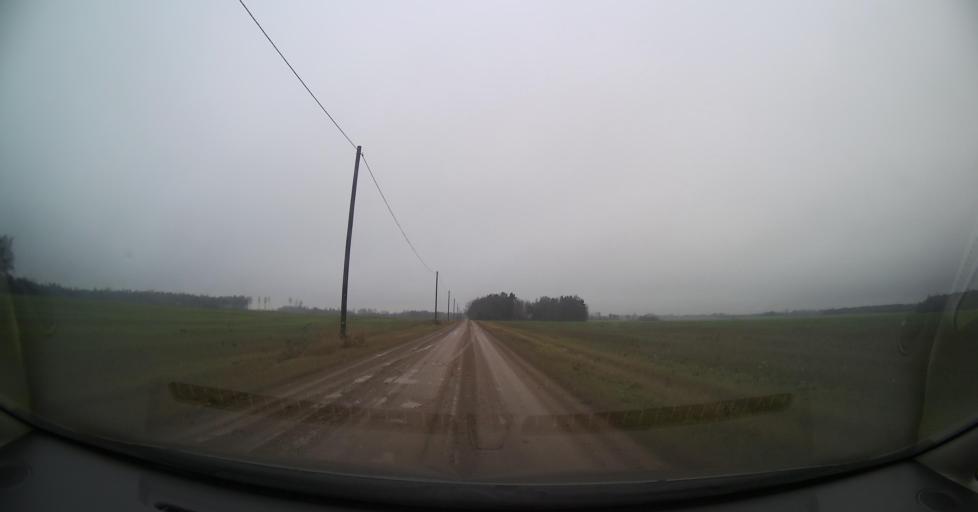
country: EE
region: Tartu
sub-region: Tartu linn
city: Tartu
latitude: 58.3798
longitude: 26.9263
